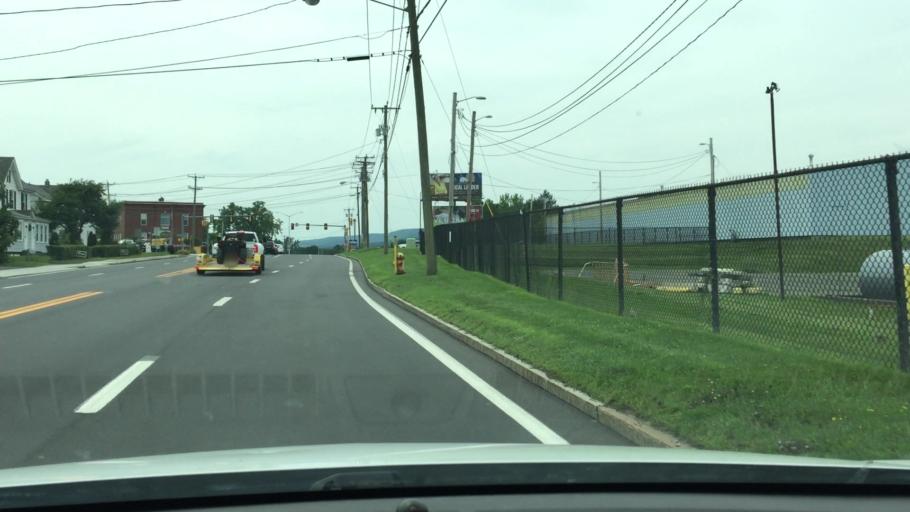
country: US
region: Massachusetts
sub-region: Berkshire County
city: Pittsfield
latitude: 42.4573
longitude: -73.2121
